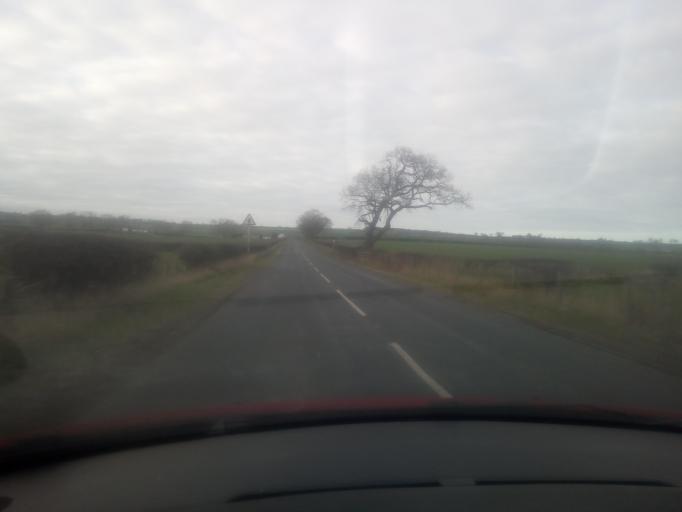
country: GB
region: England
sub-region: Darlington
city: Summerhouse
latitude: 54.5792
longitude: -1.6782
